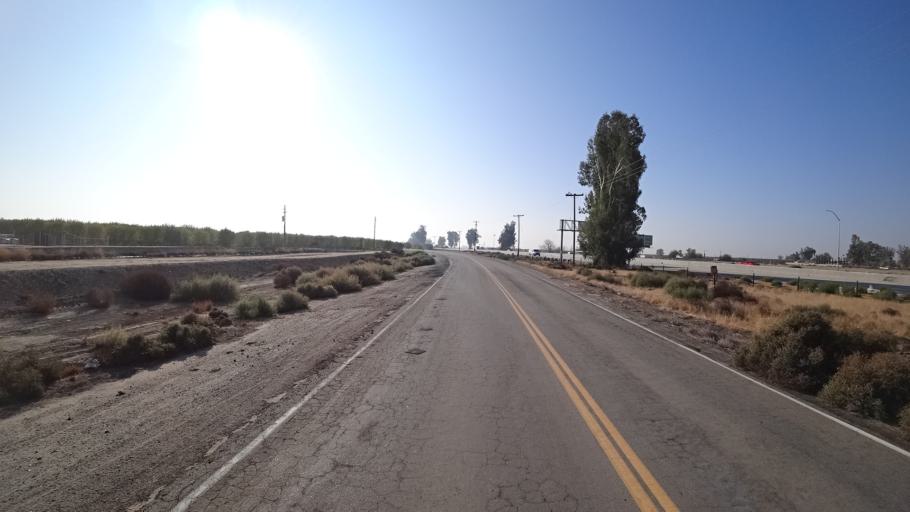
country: US
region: California
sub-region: Kern County
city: Greenfield
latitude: 35.2629
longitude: -119.0213
